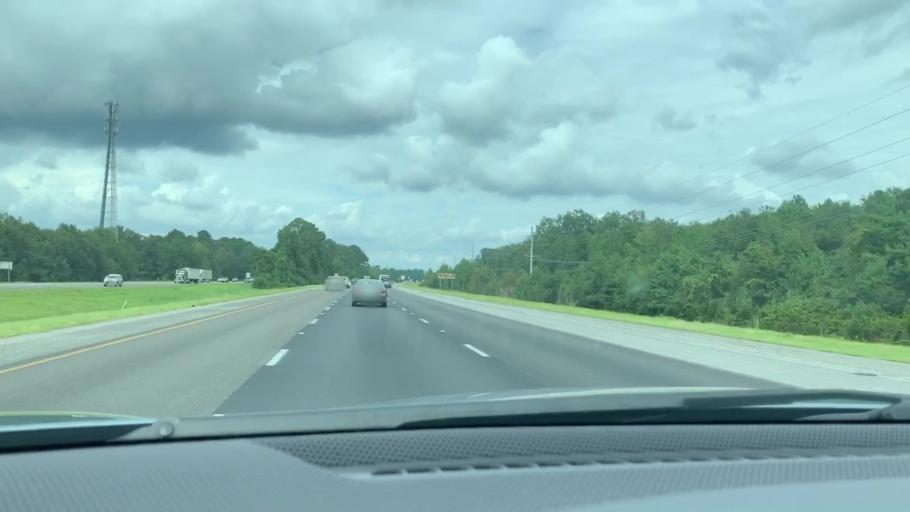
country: US
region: Georgia
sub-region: Liberty County
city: Midway
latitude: 31.7847
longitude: -81.3771
